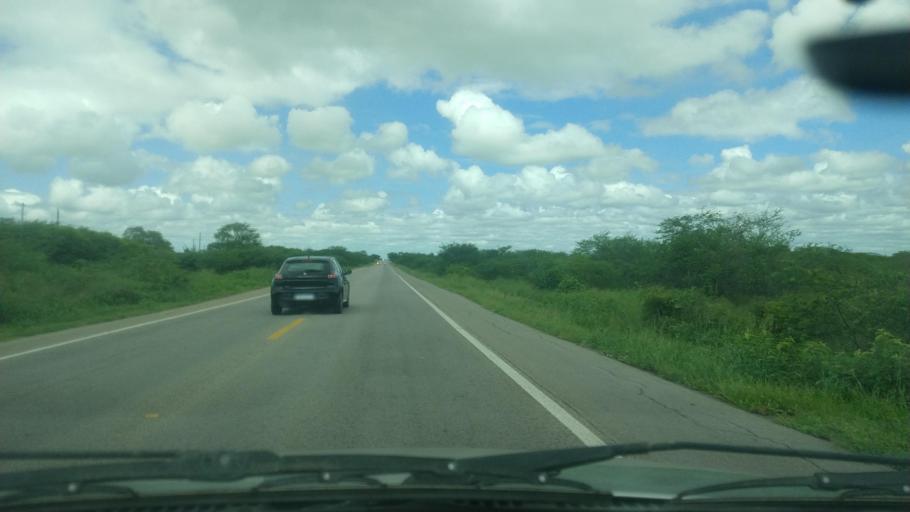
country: BR
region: Rio Grande do Norte
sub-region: Tangara
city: Tangara
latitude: -6.1650
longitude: -35.7569
